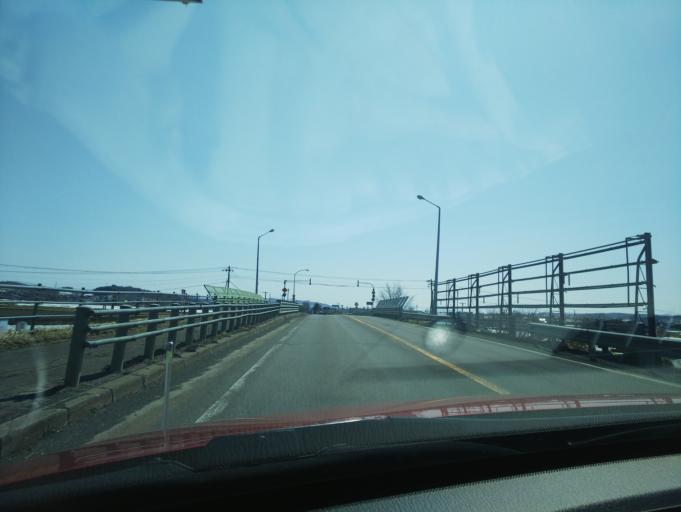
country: JP
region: Hokkaido
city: Nayoro
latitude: 44.1967
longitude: 142.3950
